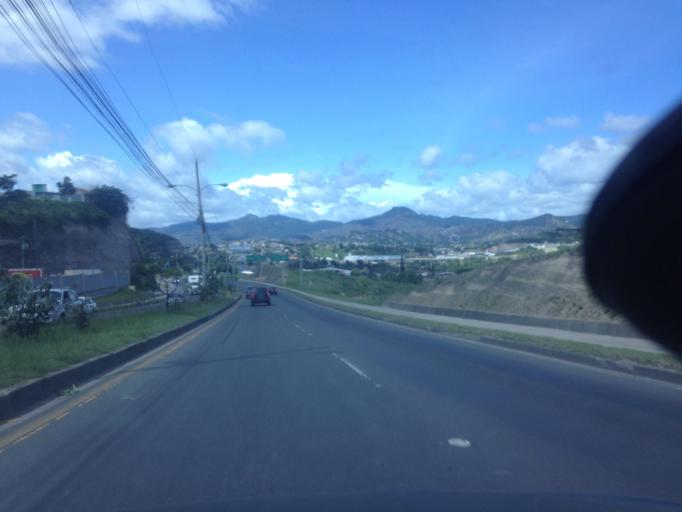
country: HN
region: Francisco Morazan
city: Yaguacire
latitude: 14.0459
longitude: -87.2167
